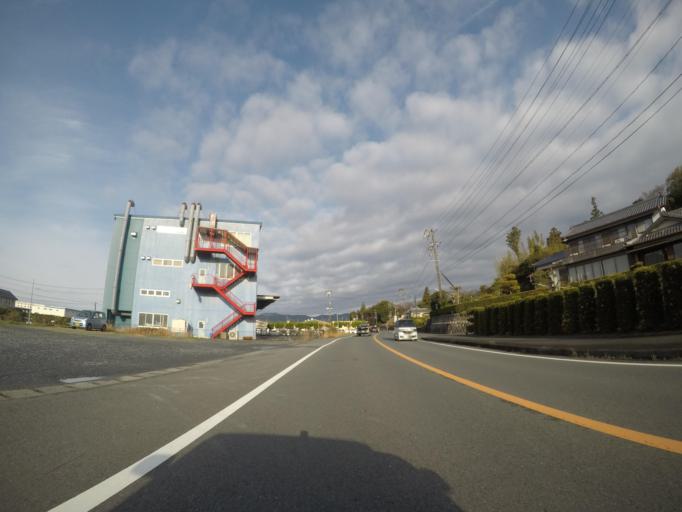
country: JP
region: Shizuoka
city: Hamakita
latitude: 34.8154
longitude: 137.6938
